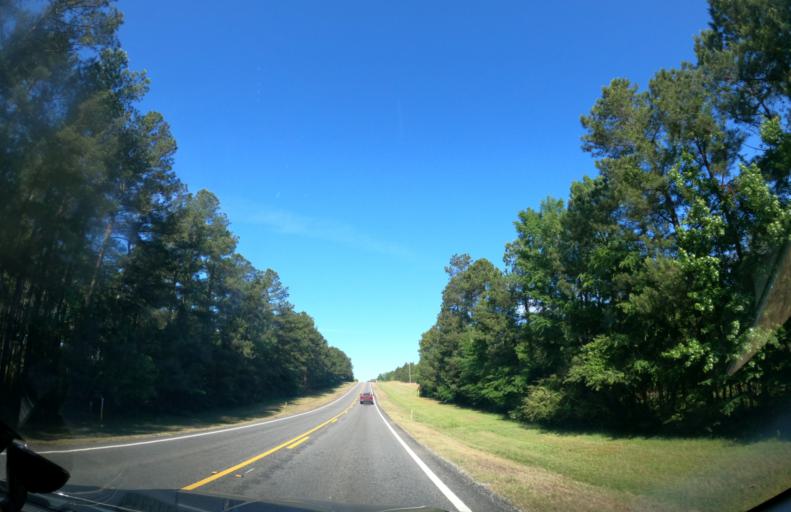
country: US
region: Georgia
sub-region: Columbia County
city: Harlem
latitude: 33.3522
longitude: -82.3313
